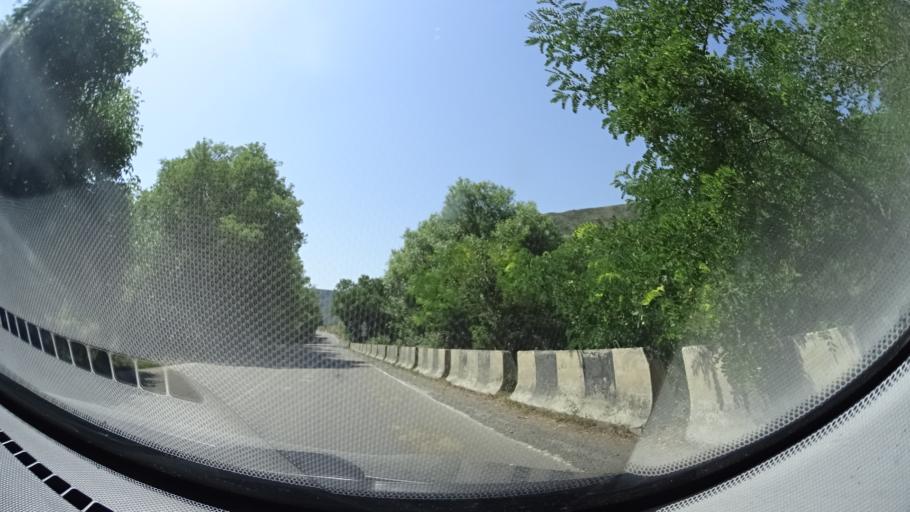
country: GE
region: Samtskhe-Javakheti
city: Aspindza
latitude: 41.4996
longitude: 43.2631
